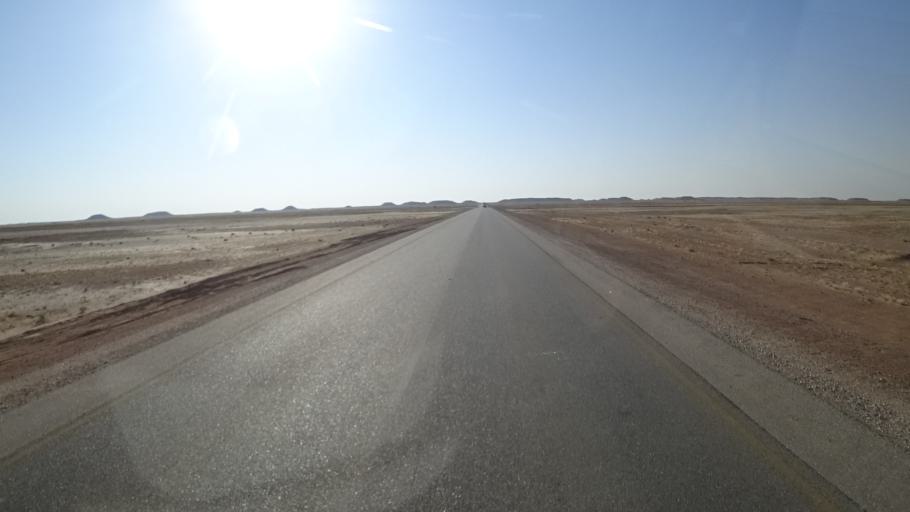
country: OM
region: Zufar
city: Salalah
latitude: 17.6419
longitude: 53.8301
